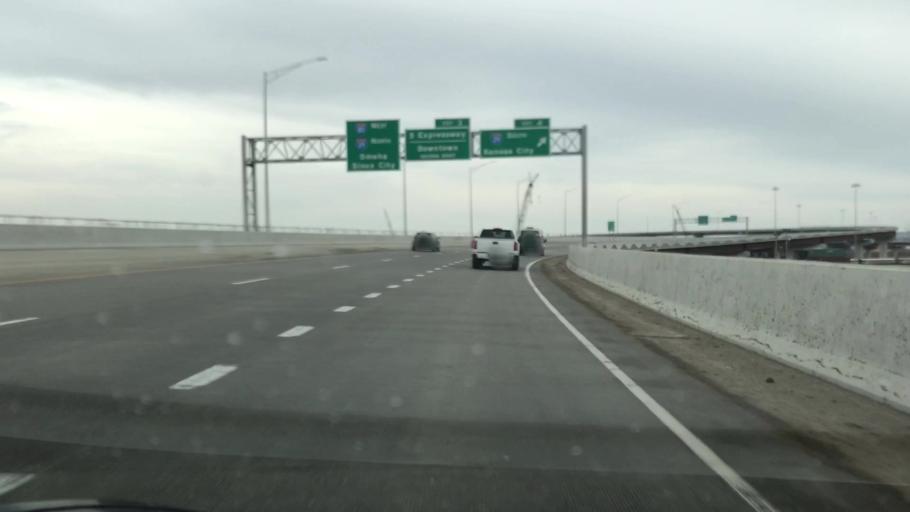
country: US
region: Iowa
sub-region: Pottawattamie County
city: Council Bluffs
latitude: 41.2328
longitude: -95.8303
